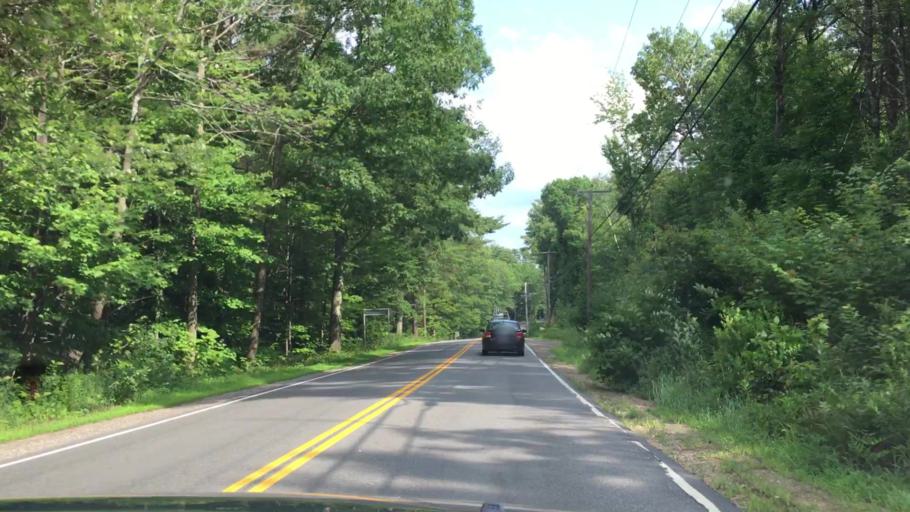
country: US
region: New Hampshire
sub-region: Belknap County
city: Gilford
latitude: 43.5860
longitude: -71.4173
